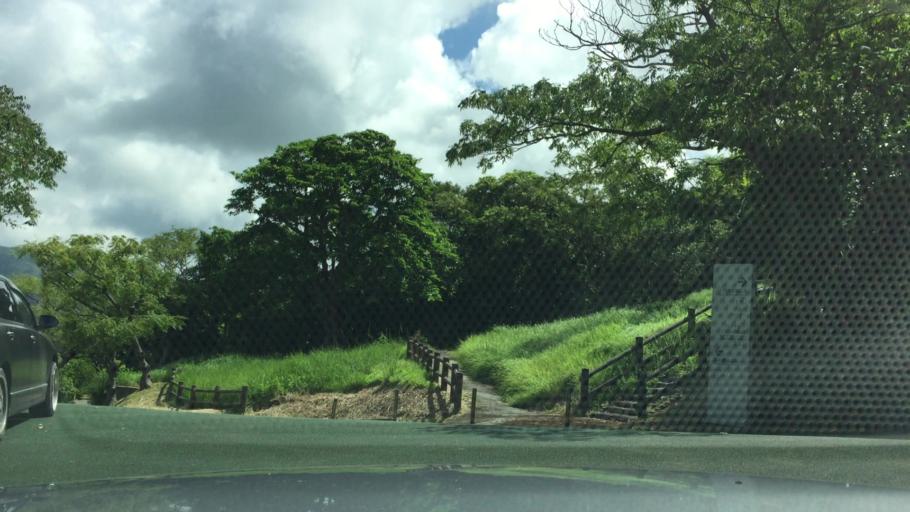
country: JP
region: Okinawa
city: Ishigaki
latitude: 24.3843
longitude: 124.1615
